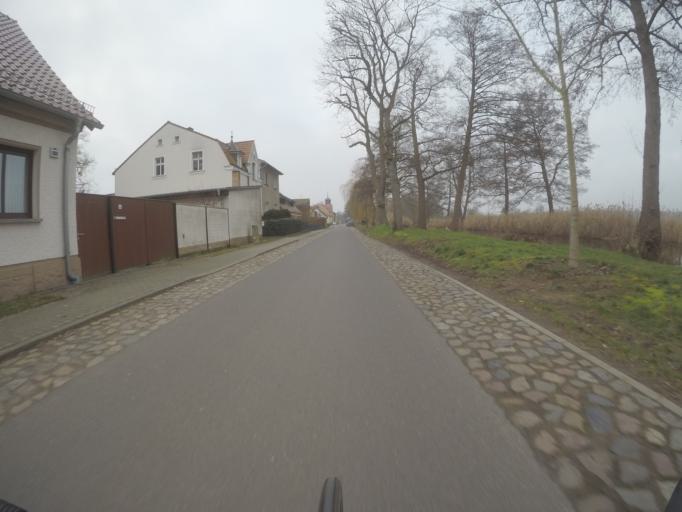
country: DE
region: Brandenburg
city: Marienwerder
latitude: 52.8561
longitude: 13.5127
